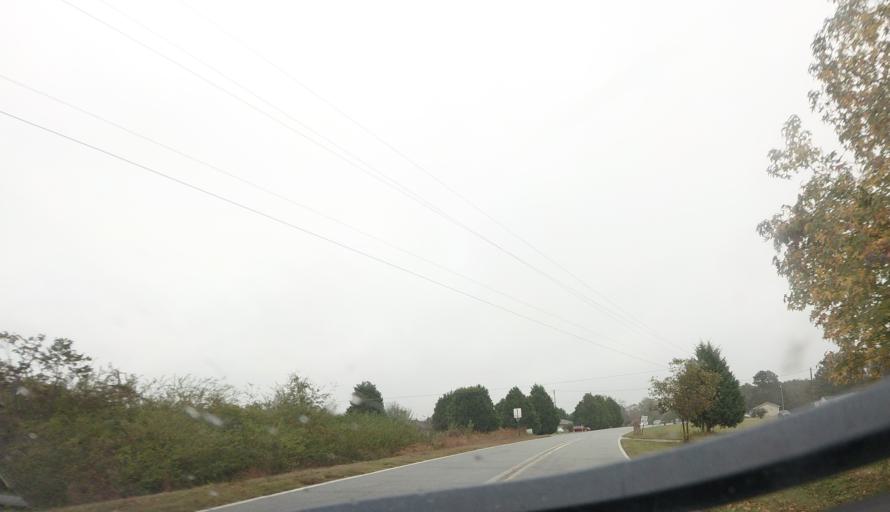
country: US
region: Georgia
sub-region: Peach County
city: Fort Valley
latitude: 32.5459
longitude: -83.9168
